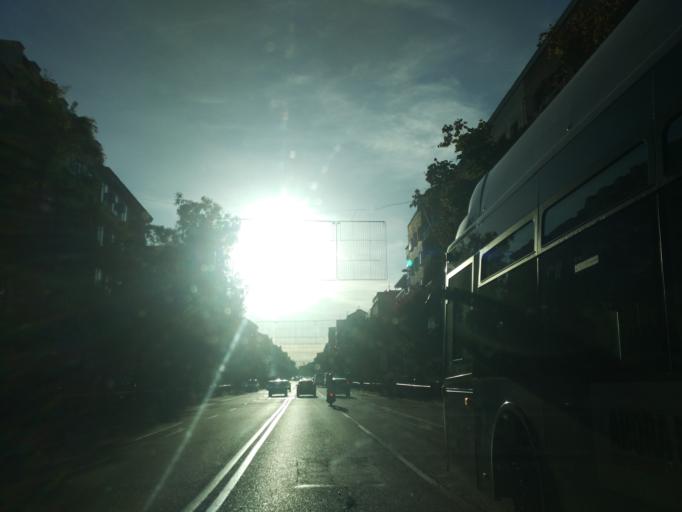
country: ES
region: Madrid
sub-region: Provincia de Madrid
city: Carabanchel
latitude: 40.3955
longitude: -3.7199
